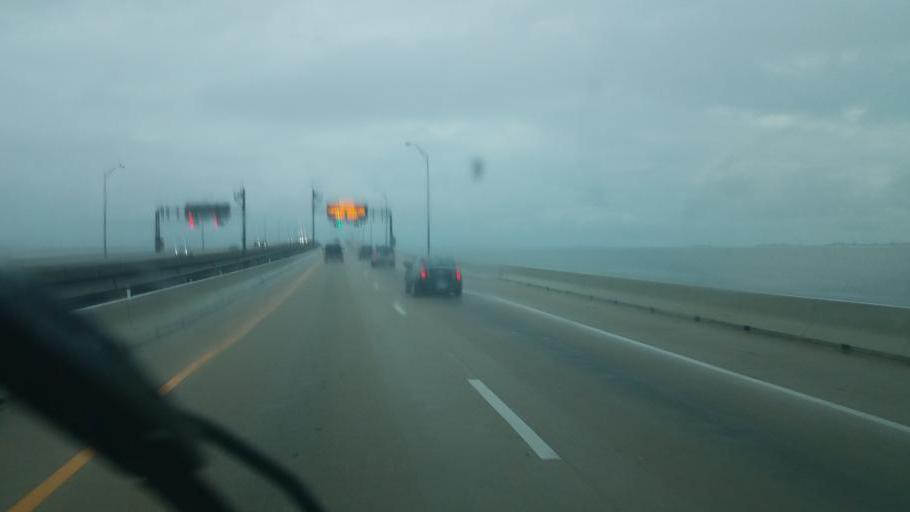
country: US
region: Virginia
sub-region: City of Newport News
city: Newport News
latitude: 36.9155
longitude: -76.4155
